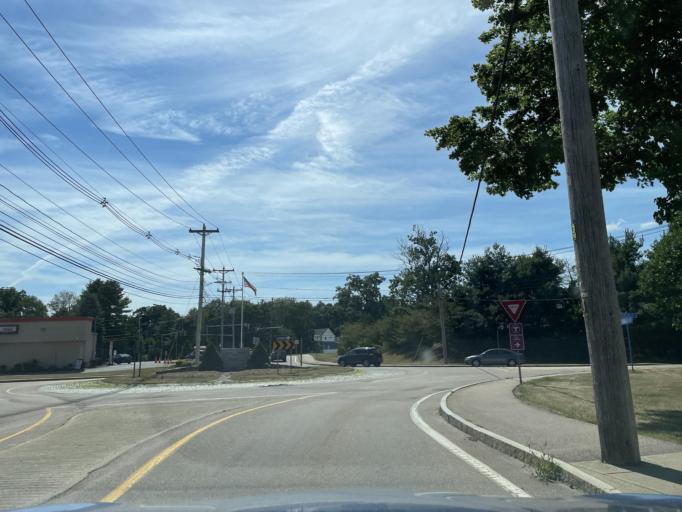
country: US
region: Massachusetts
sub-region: Norfolk County
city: Foxborough
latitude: 42.0747
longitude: -71.2589
